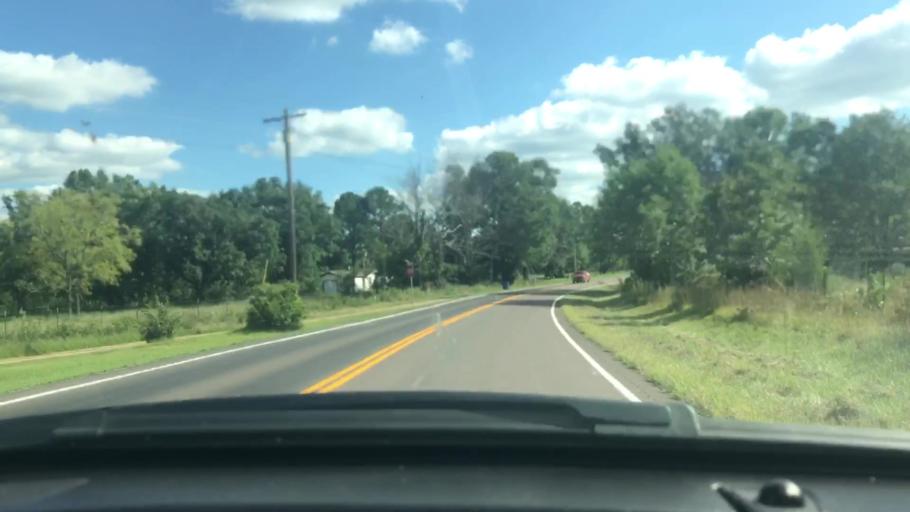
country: US
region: Missouri
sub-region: Wright County
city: Mountain Grove
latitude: 37.2285
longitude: -92.2931
